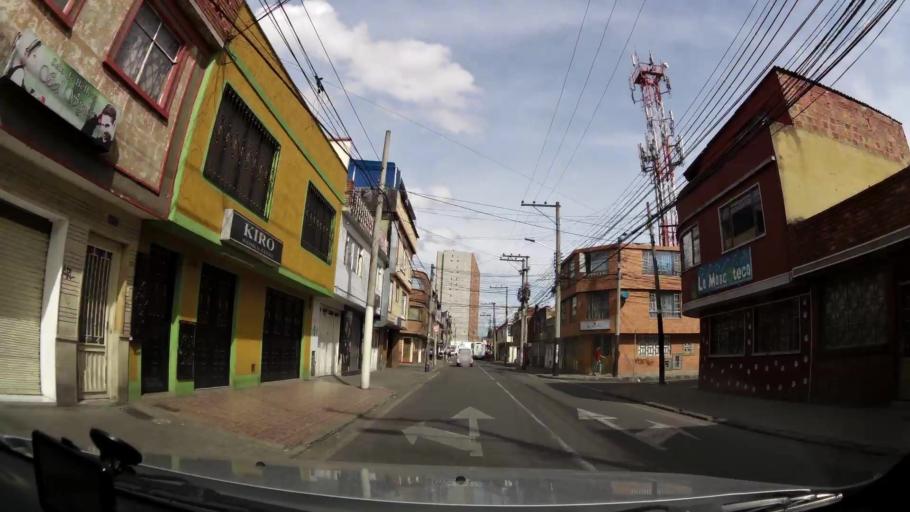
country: CO
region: Bogota D.C.
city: Bogota
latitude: 4.6772
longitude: -74.0950
